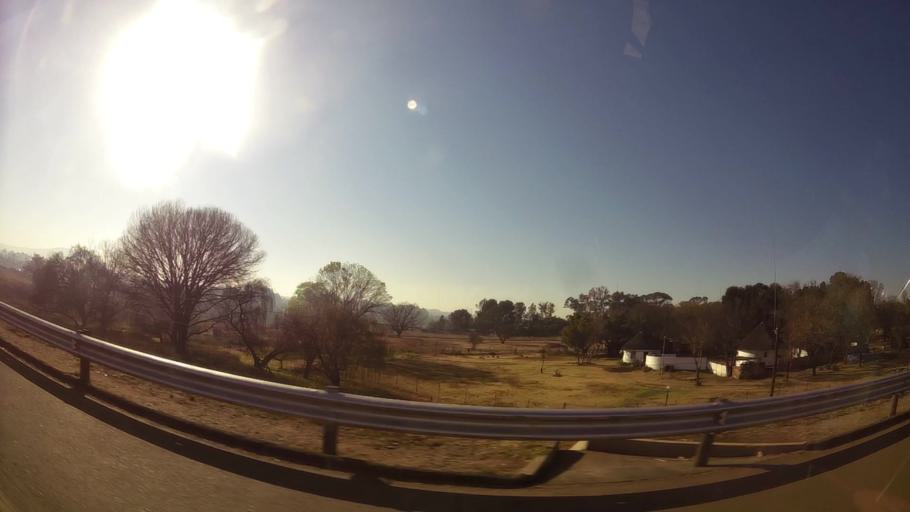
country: ZA
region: Gauteng
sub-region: City of Tshwane Metropolitan Municipality
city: Centurion
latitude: -25.8497
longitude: 28.1085
